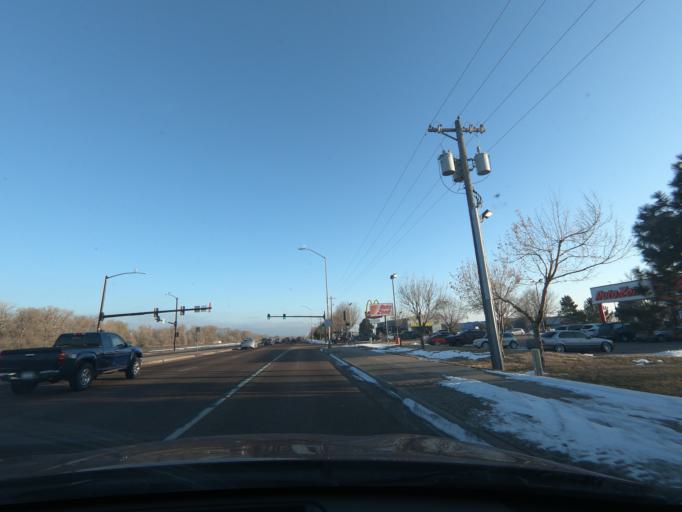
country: US
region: Colorado
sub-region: El Paso County
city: Security-Widefield
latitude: 38.7429
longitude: -104.7367
